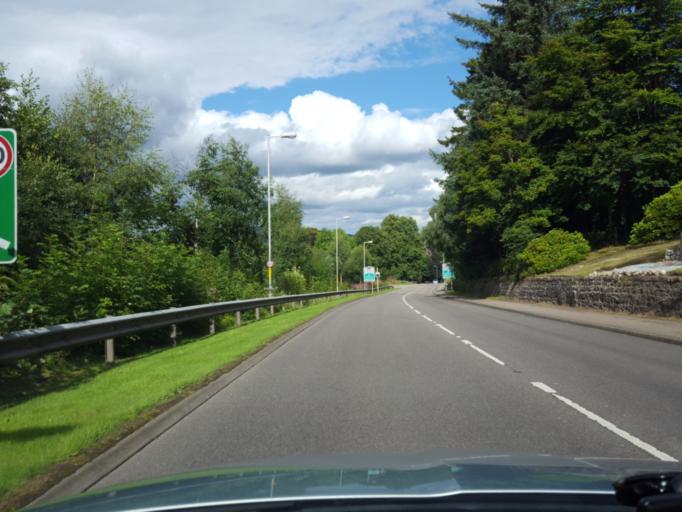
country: GB
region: Scotland
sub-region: Moray
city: Rothes
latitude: 57.4668
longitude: -3.2333
